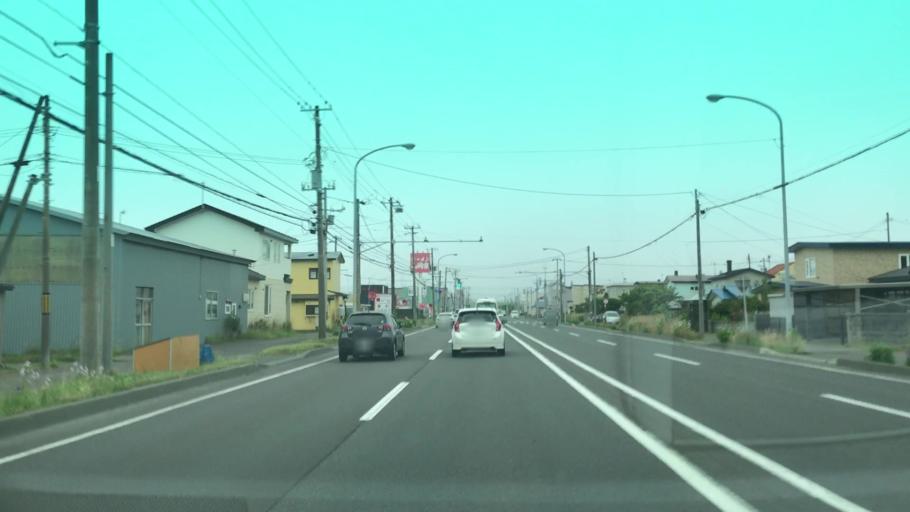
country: JP
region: Hokkaido
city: Muroran
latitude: 42.3649
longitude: 141.0581
